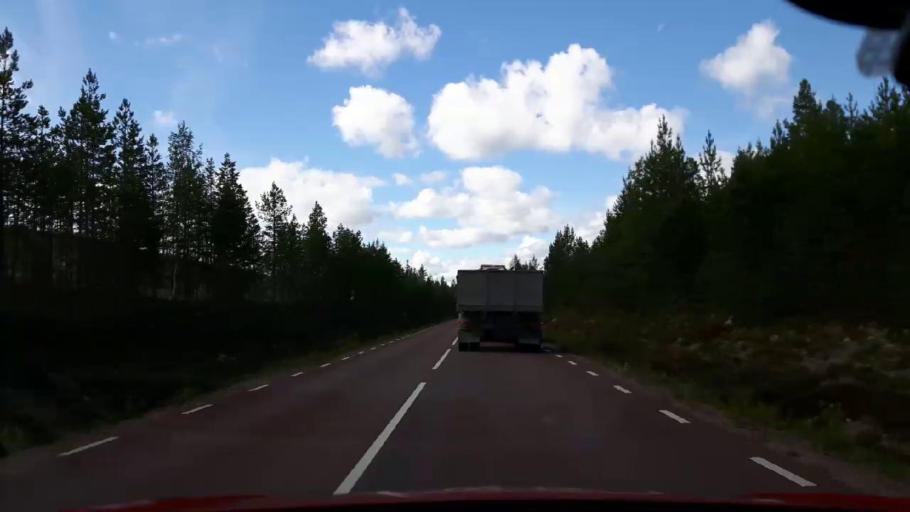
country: SE
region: Jaemtland
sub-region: Harjedalens Kommun
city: Sveg
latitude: 62.0063
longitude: 14.3002
